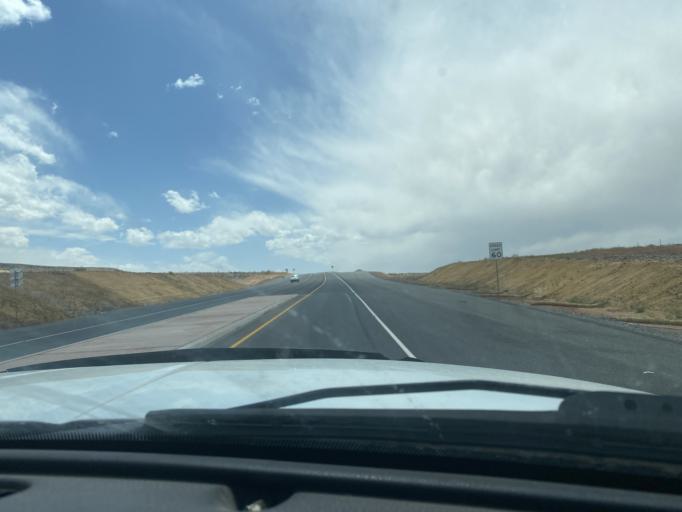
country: US
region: Utah
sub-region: Washington County
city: Hurricane
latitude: 37.1675
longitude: -113.3460
